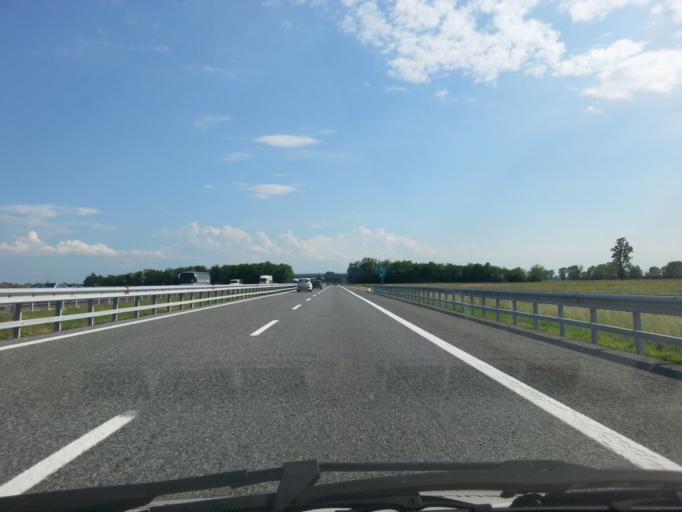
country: IT
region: Piedmont
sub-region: Provincia di Cuneo
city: Caramagna Piemonte
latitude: 44.7614
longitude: 7.7505
